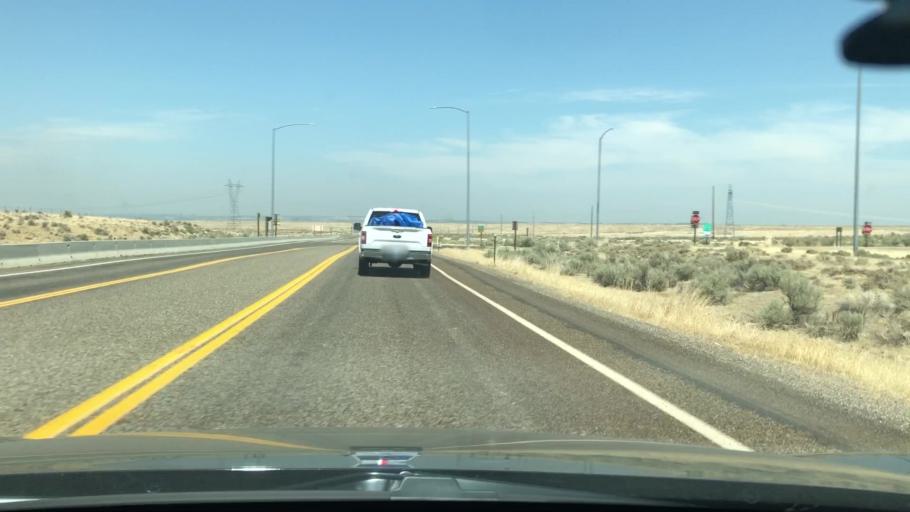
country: US
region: Idaho
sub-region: Owyhee County
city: Marsing
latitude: 43.4648
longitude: -116.8660
